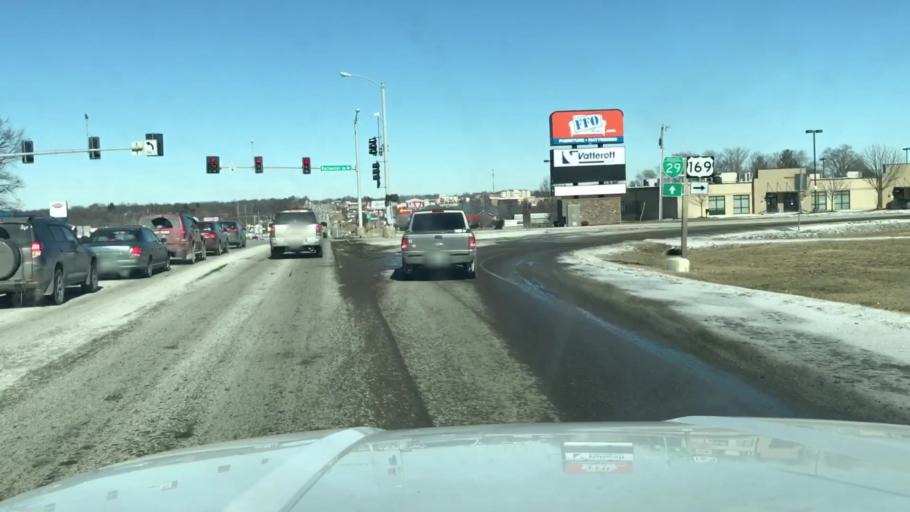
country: US
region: Missouri
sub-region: Andrew County
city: Country Club Village
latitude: 39.8025
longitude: -94.8150
